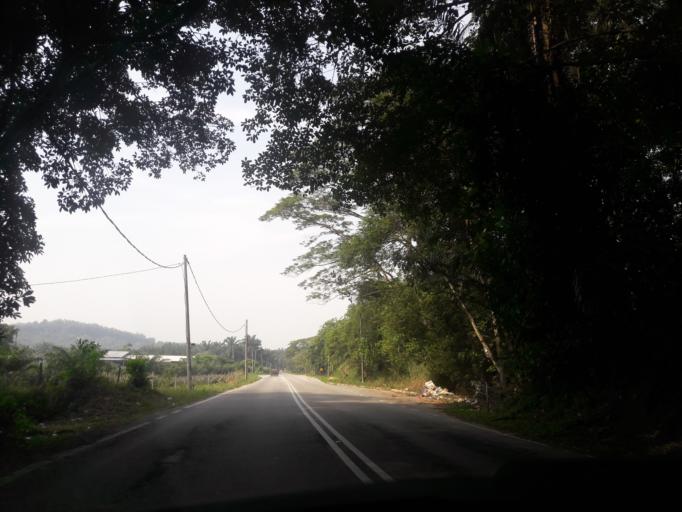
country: MY
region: Kedah
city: Kulim
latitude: 5.3518
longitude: 100.5201
